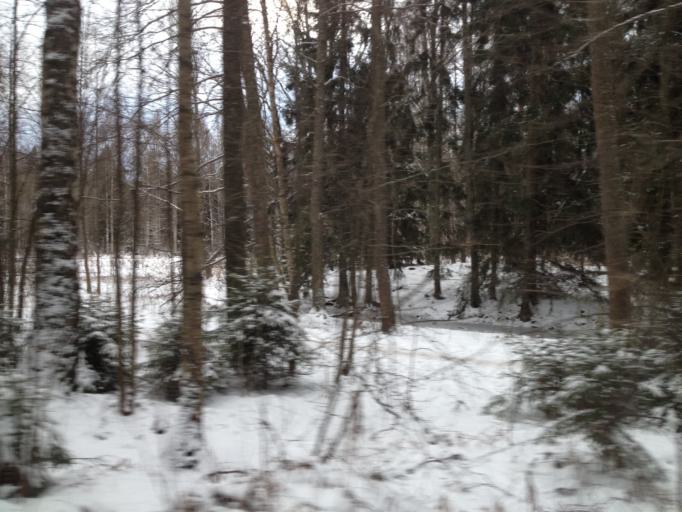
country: FI
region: Uusimaa
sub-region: Helsinki
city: Vantaa
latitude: 60.2019
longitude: 25.1682
